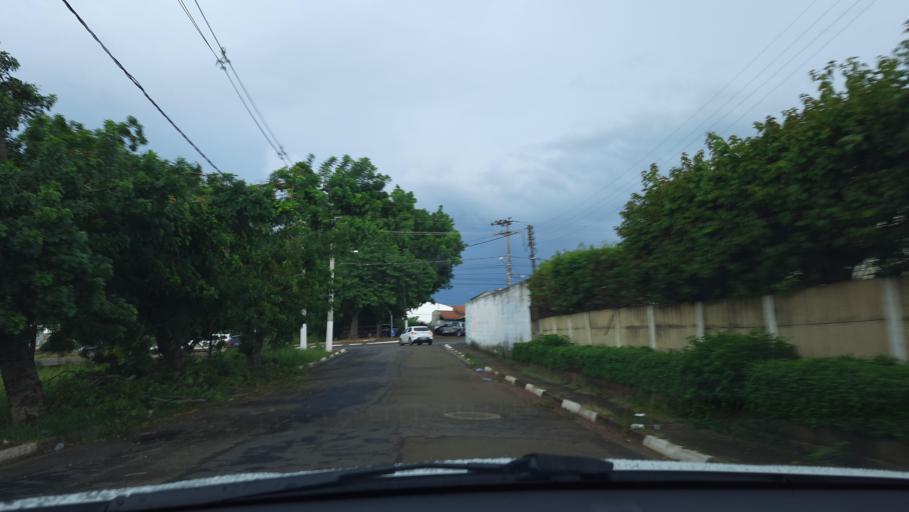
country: BR
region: Sao Paulo
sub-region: Casa Branca
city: Casa Branca
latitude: -21.7802
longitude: -47.0716
